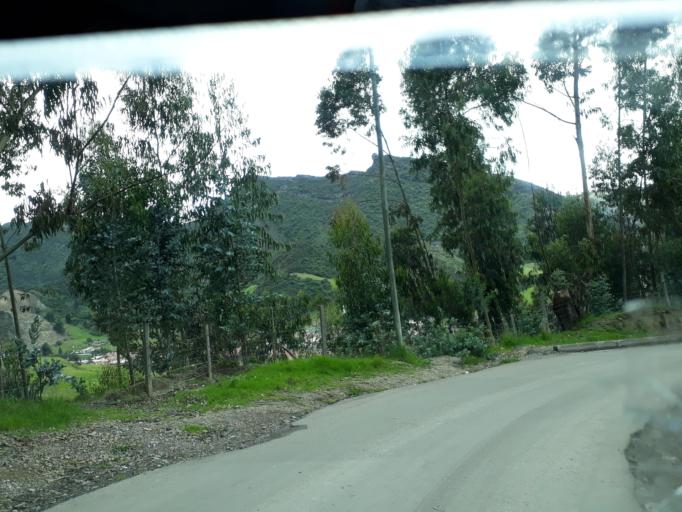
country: CO
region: Cundinamarca
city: Sutatausa
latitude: 5.1978
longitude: -73.8908
